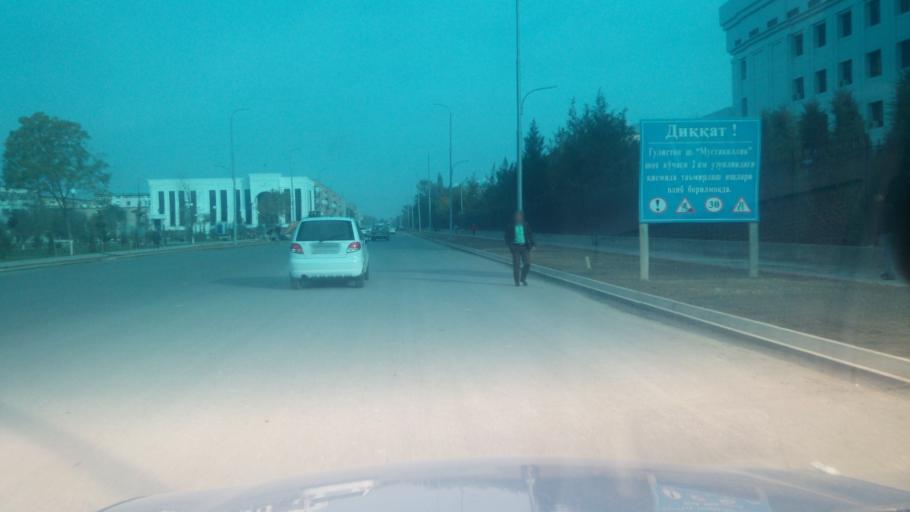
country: UZ
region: Sirdaryo
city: Guliston
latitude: 40.4995
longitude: 68.7761
